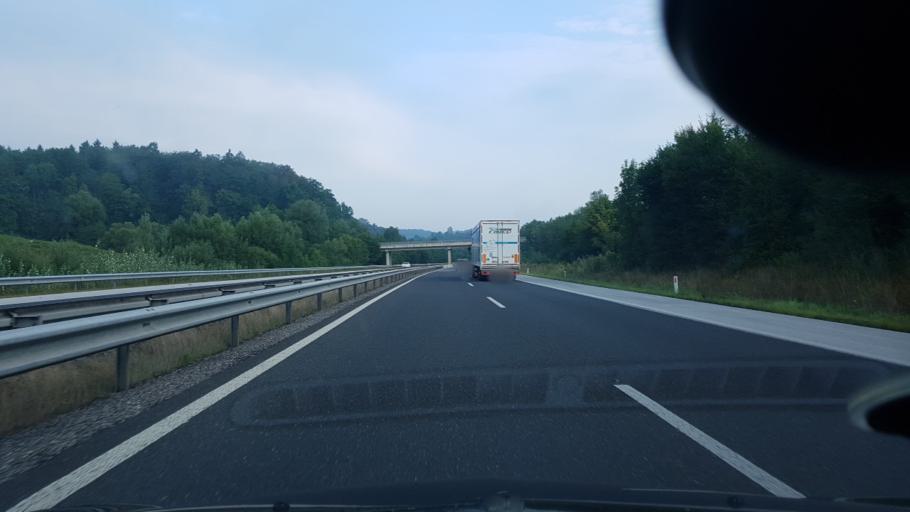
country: SI
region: Kungota
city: Zgornja Kungota
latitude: 46.6416
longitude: 15.6518
